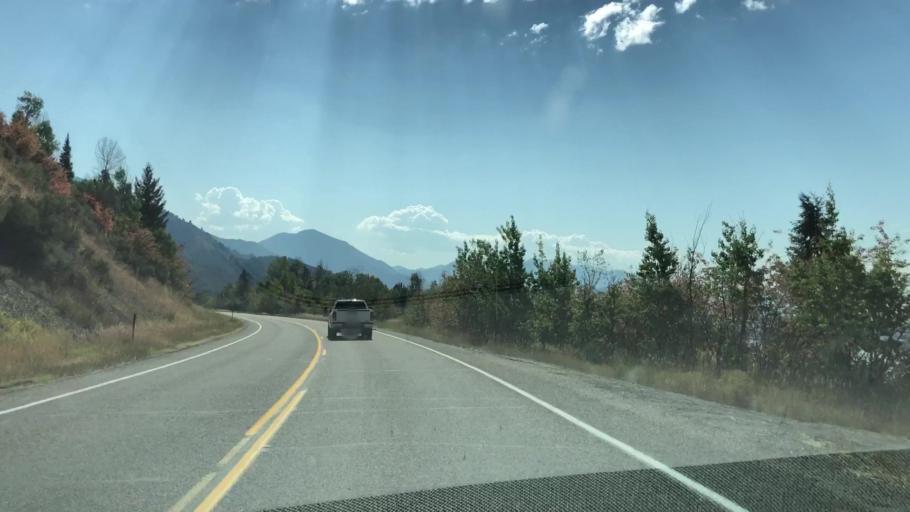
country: US
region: Wyoming
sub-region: Teton County
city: Hoback
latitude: 43.2281
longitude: -111.0868
